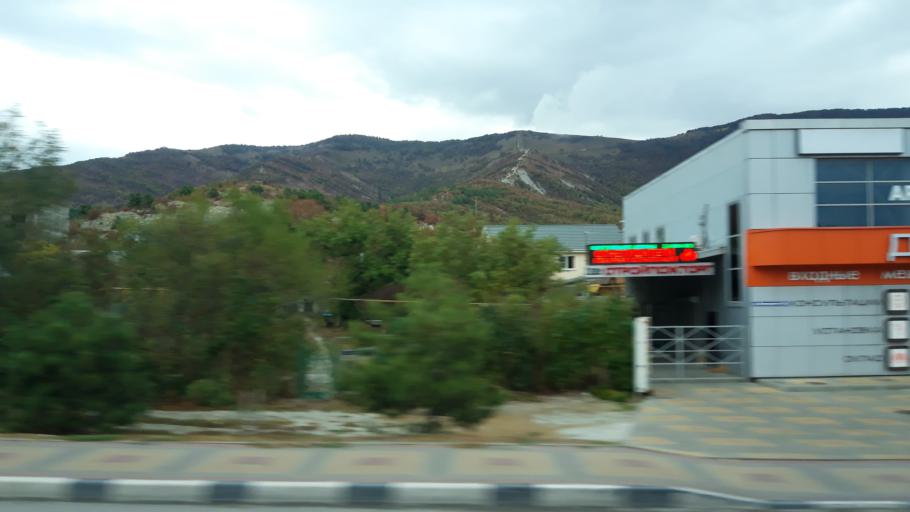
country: RU
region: Krasnodarskiy
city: Gelendzhik
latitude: 44.5923
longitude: 38.0486
